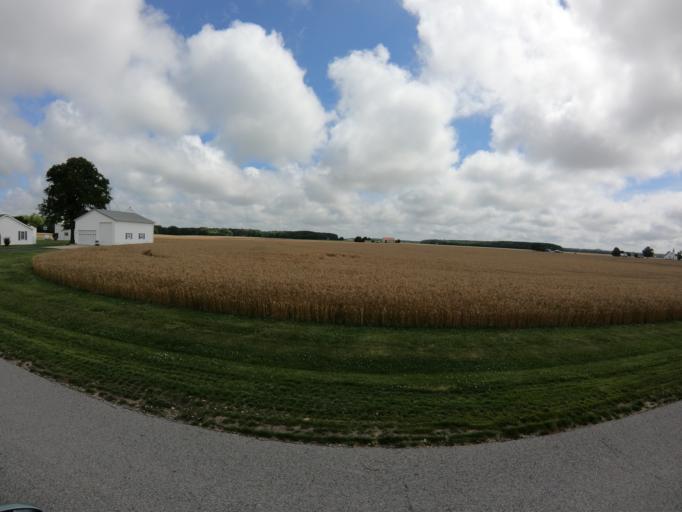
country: US
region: Maryland
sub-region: Caroline County
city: Greensboro
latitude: 39.0954
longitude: -75.8820
